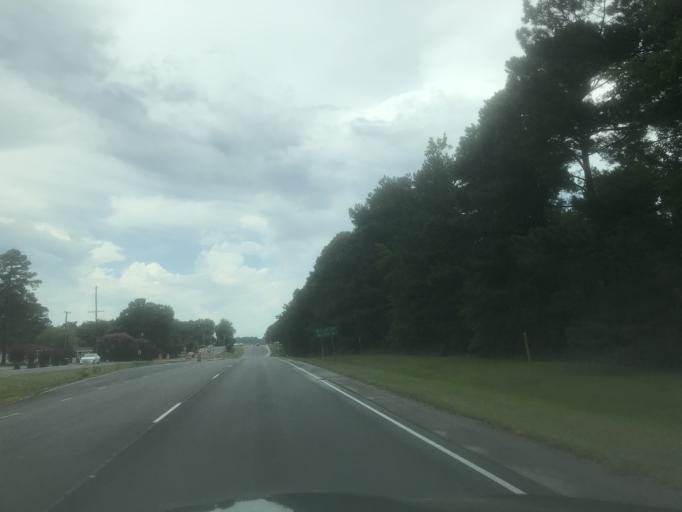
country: US
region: North Carolina
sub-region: Johnston County
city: Clayton
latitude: 35.6344
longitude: -78.4387
